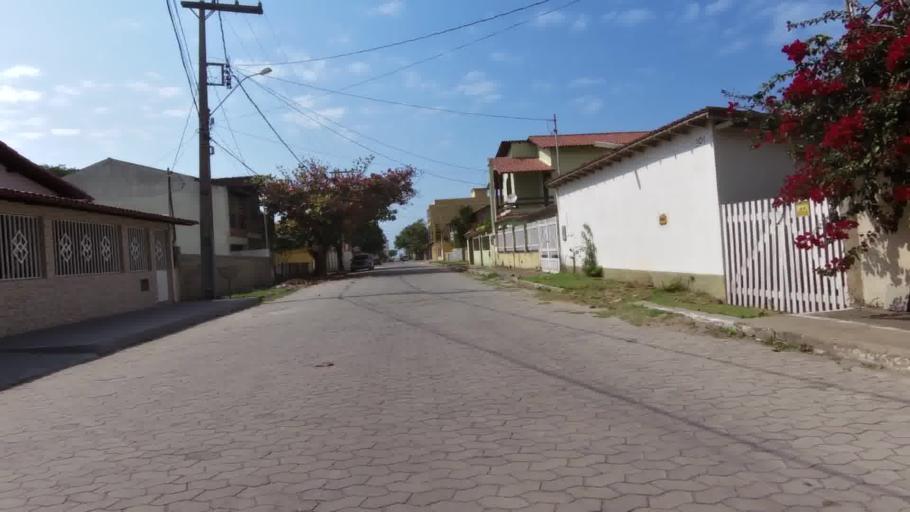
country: BR
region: Espirito Santo
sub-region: Marataizes
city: Marataizes
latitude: -21.0324
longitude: -40.8163
